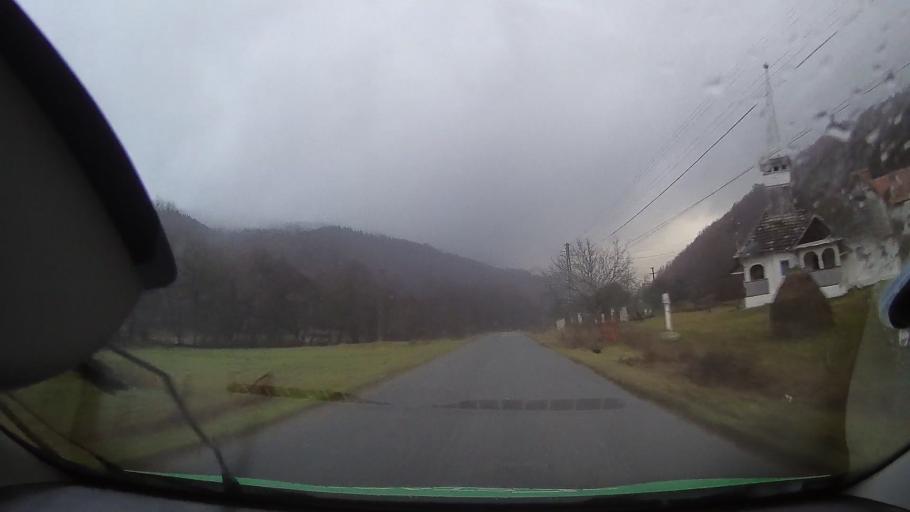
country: RO
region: Hunedoara
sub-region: Comuna Ribita
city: Ribita
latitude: 46.2587
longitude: 22.7456
